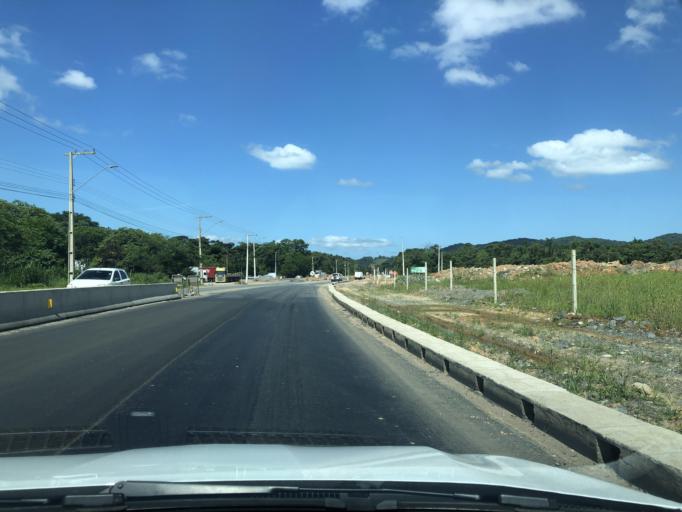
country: BR
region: Santa Catarina
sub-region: Joinville
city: Joinville
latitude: -26.2509
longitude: -48.8656
